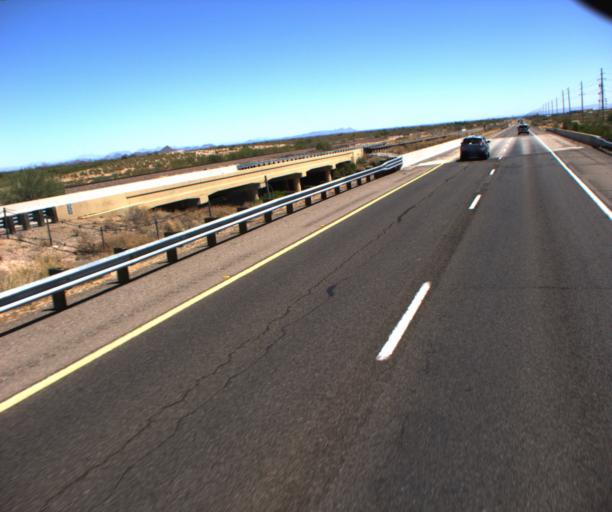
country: US
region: Arizona
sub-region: Maricopa County
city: Sun City West
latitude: 33.7479
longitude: -112.4904
